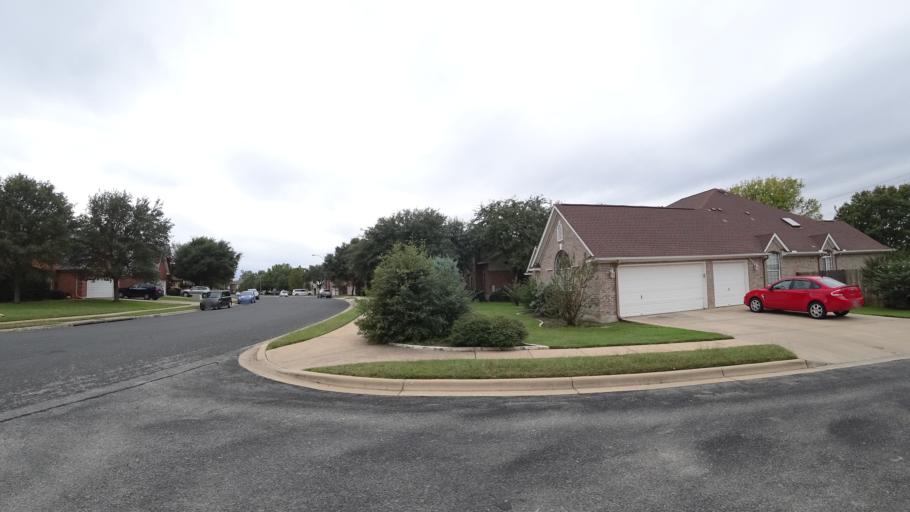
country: US
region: Texas
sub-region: Williamson County
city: Brushy Creek
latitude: 30.5003
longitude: -97.7470
